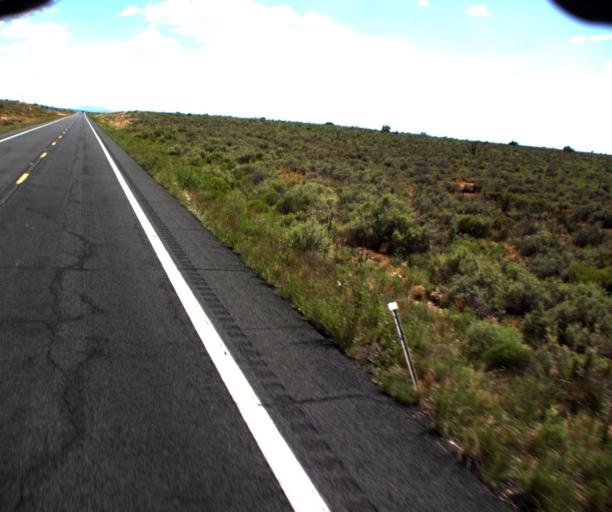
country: US
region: Arizona
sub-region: Coconino County
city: Williams
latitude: 35.6338
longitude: -112.1420
